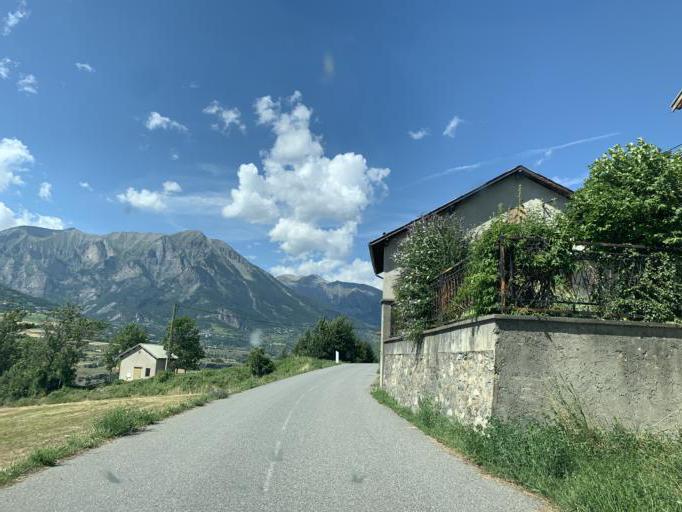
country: FR
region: Provence-Alpes-Cote d'Azur
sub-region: Departement des Hautes-Alpes
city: Embrun
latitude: 44.5820
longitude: 6.5286
